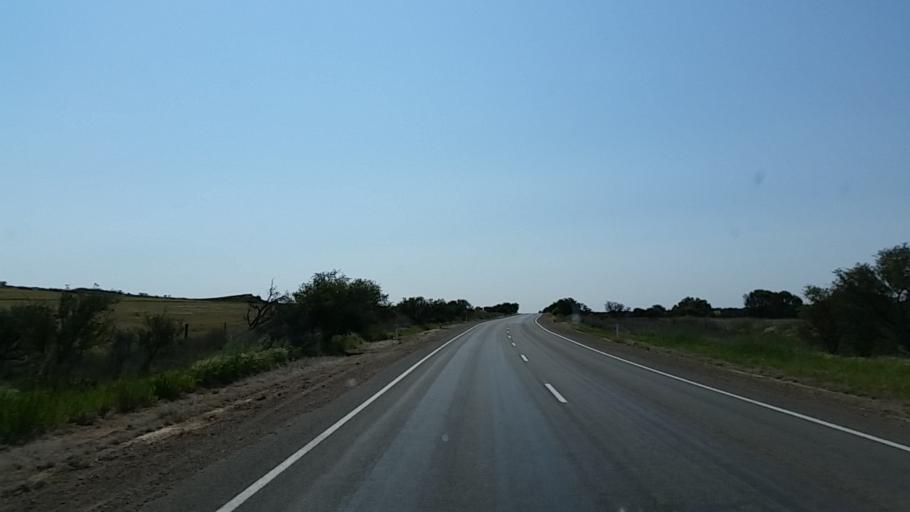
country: AU
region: South Australia
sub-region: Port Pirie City and Dists
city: Crystal Brook
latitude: -33.2425
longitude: 138.3765
